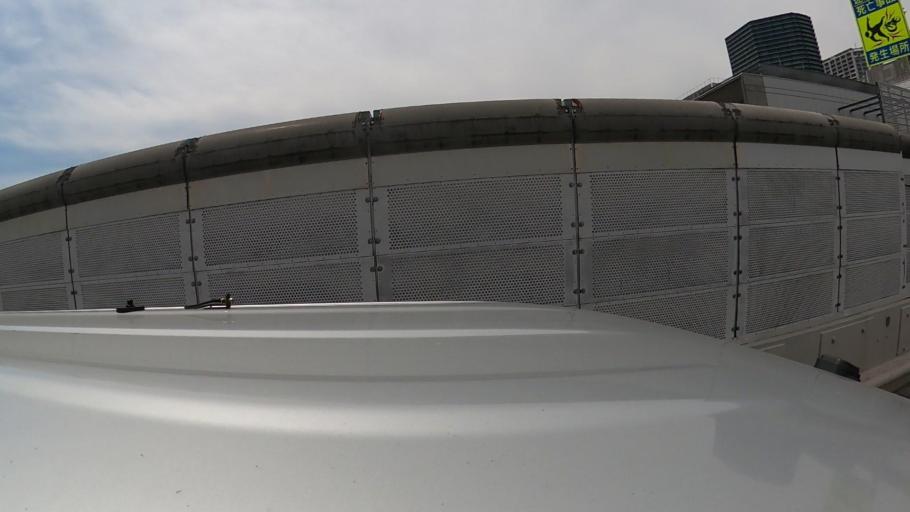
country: JP
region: Tokyo
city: Tokyo
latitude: 35.6287
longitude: 139.7504
